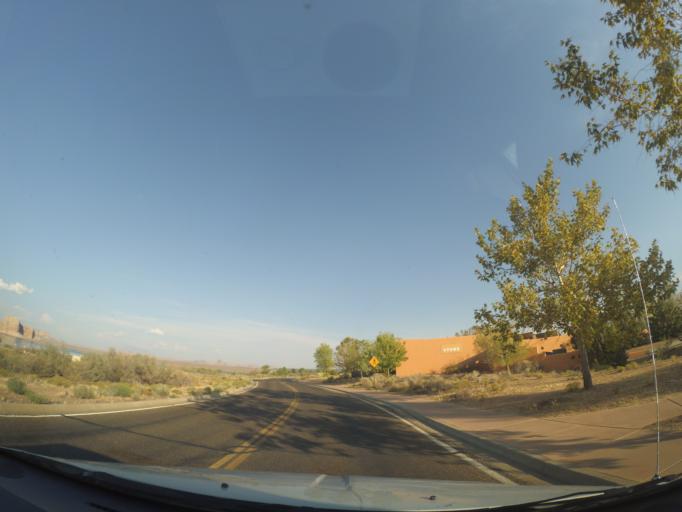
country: US
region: Arizona
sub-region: Coconino County
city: Page
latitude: 36.9993
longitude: -111.4984
